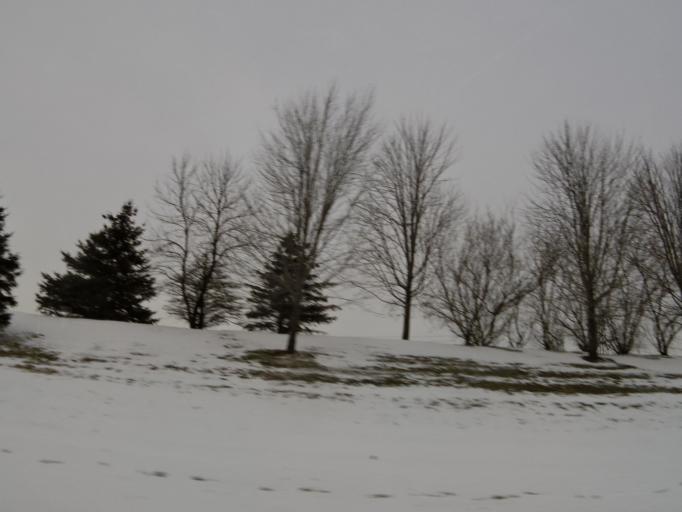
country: US
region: Minnesota
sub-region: Washington County
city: Stillwater
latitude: 45.0320
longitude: -92.8370
